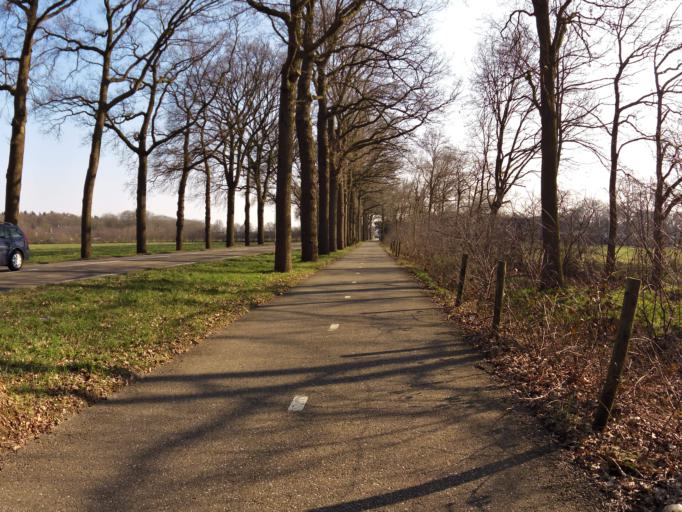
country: NL
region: North Brabant
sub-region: Gemeente Maasdonk
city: Geffen
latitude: 51.7181
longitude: 5.4011
